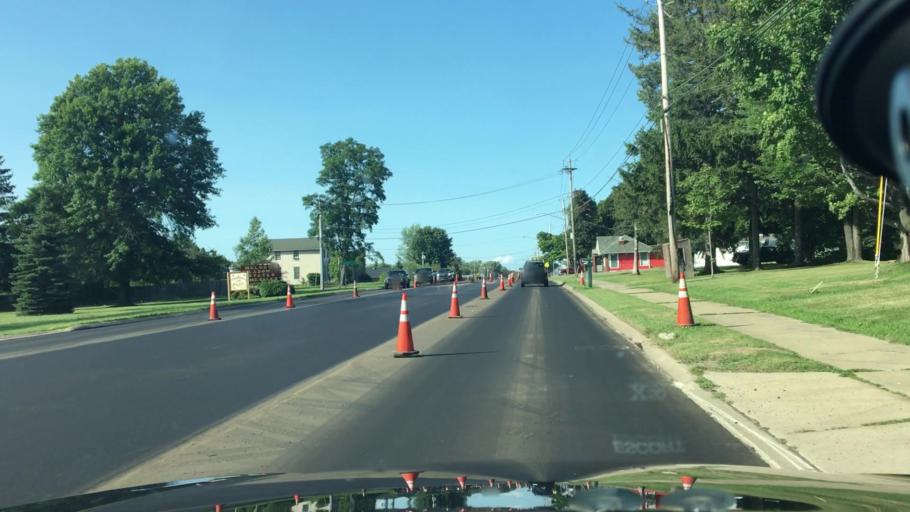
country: US
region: New York
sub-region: Erie County
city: Angola on the Lake
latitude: 42.6413
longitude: -79.0462
